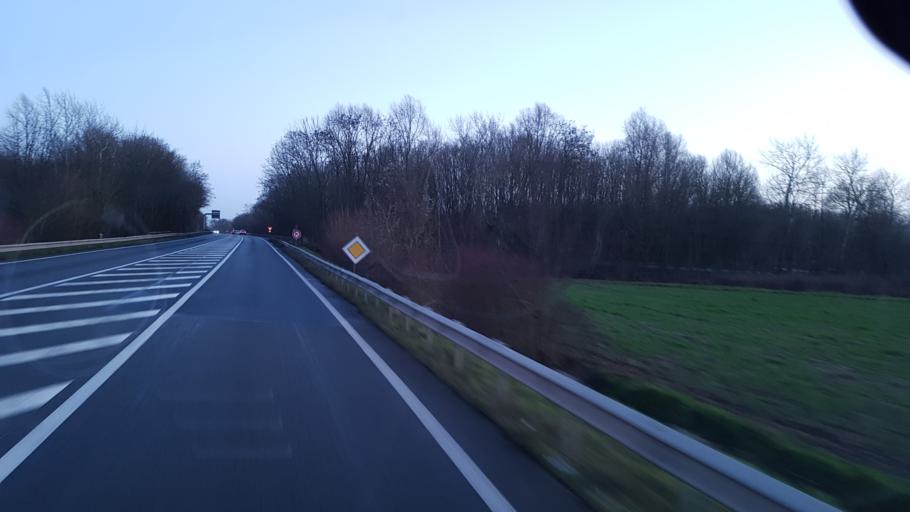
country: FR
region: Nord-Pas-de-Calais
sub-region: Departement du Nord
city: Cuincy
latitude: 50.3585
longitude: 3.0445
